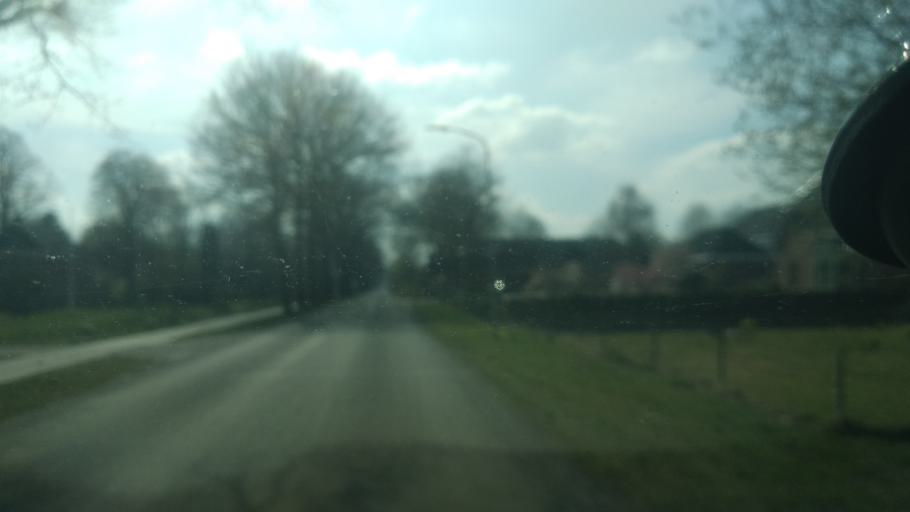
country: NL
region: Groningen
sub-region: Gemeente Stadskanaal
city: Stadskanaal
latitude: 52.9747
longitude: 6.8920
